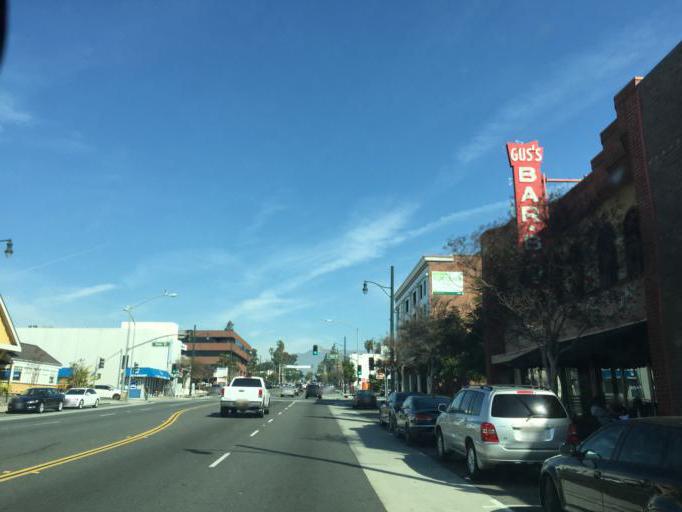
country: US
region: California
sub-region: Los Angeles County
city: South Pasadena
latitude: 34.1162
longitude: -118.1503
